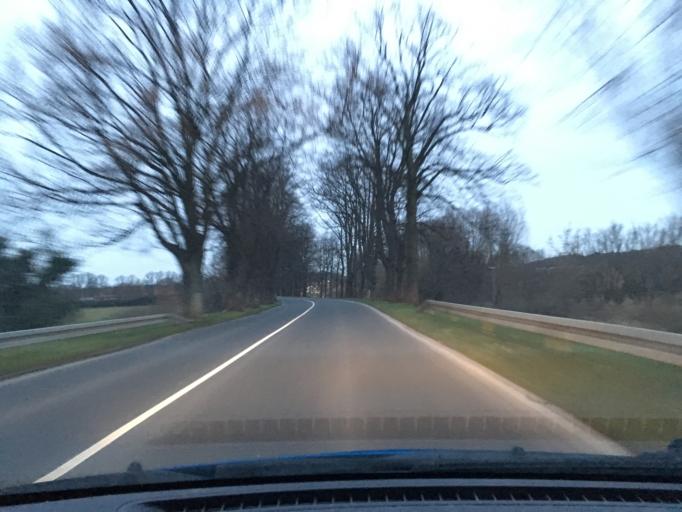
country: DE
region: Mecklenburg-Vorpommern
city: Boizenburg
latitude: 53.3730
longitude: 10.7327
